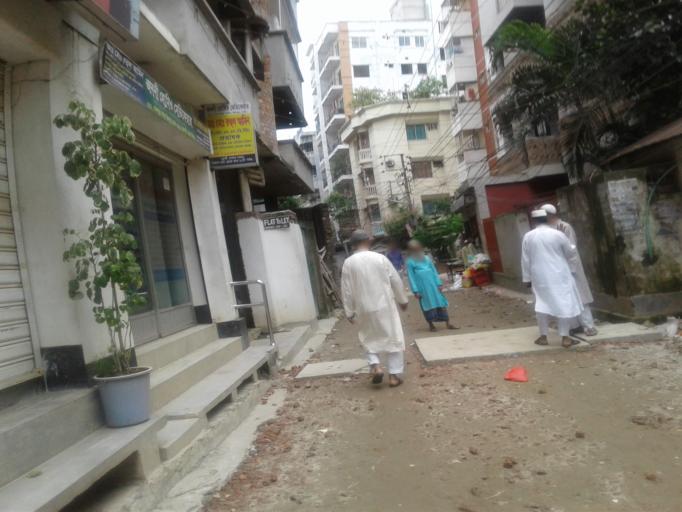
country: BD
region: Dhaka
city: Azimpur
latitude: 23.8024
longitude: 90.3763
